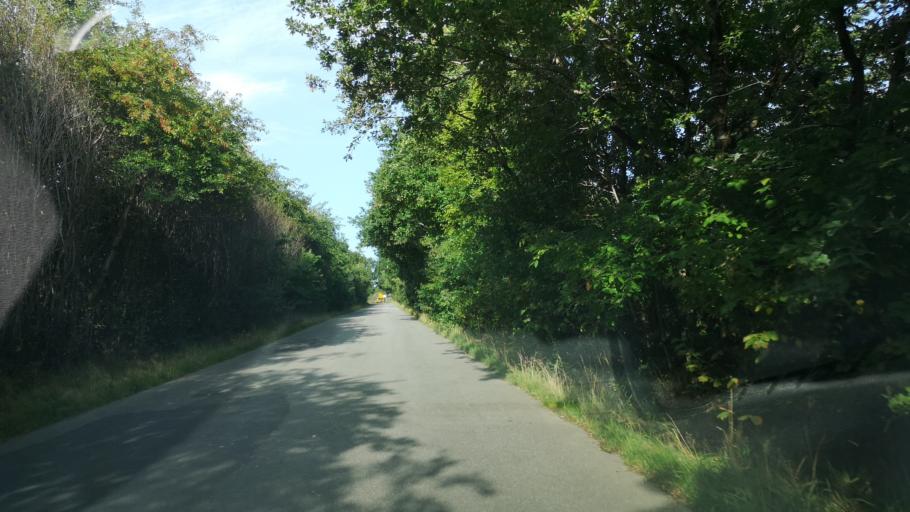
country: DK
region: Central Jutland
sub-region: Ikast-Brande Kommune
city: Ikast
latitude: 56.1511
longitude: 9.1325
